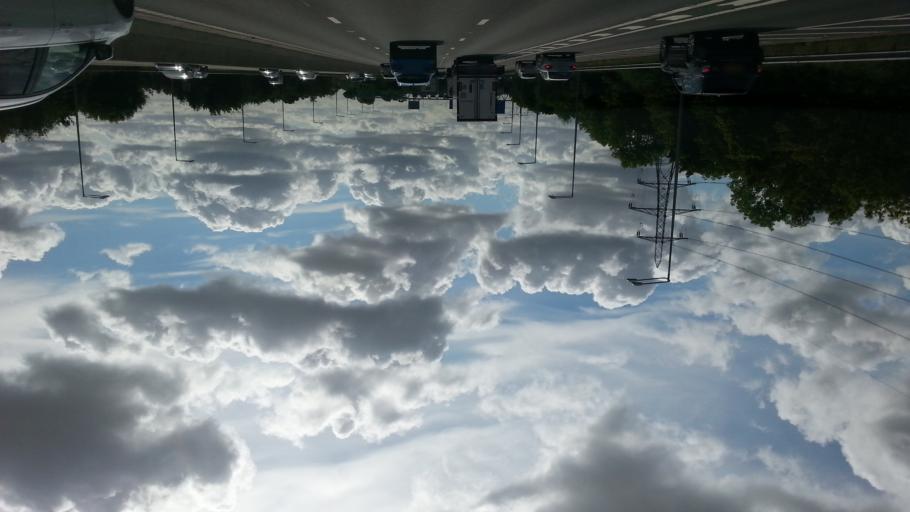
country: GB
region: England
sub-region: Essex
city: Theydon Bois
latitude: 51.6823
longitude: 0.1110
